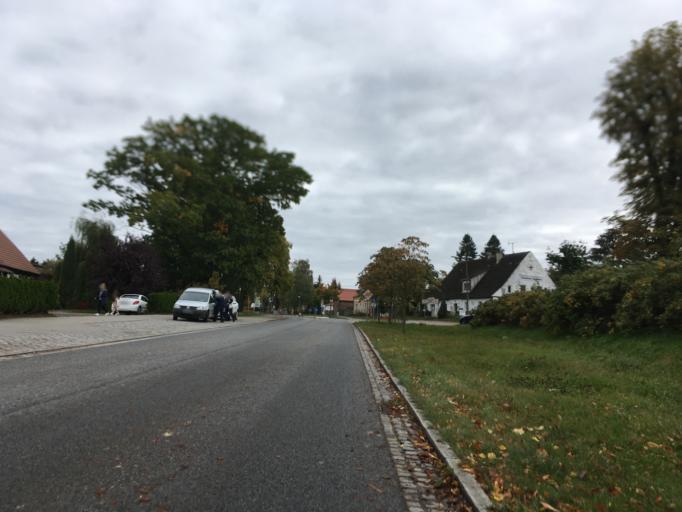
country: DE
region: Brandenburg
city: Werftpfuhl
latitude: 52.7028
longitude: 13.8827
